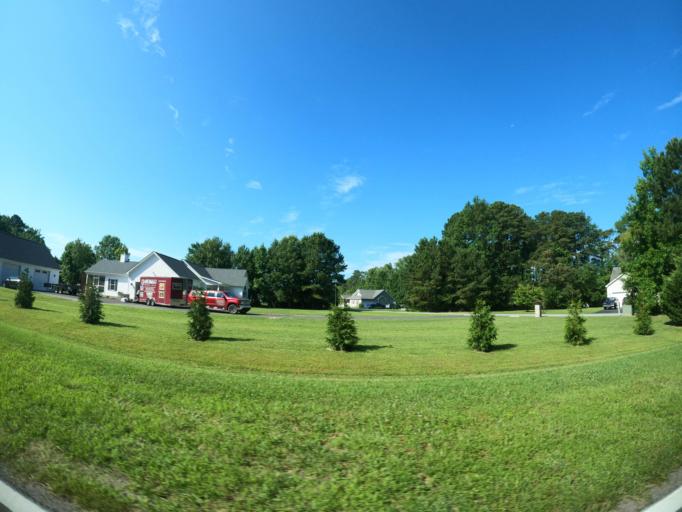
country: US
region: Delaware
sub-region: Sussex County
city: Ocean View
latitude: 38.4906
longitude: -75.1228
